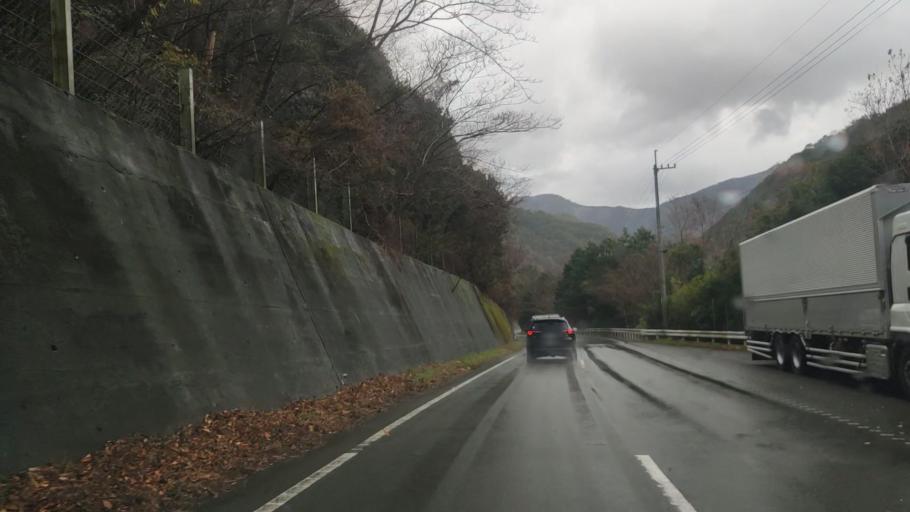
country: JP
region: Tokushima
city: Kamojimacho-jogejima
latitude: 34.1658
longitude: 134.3402
